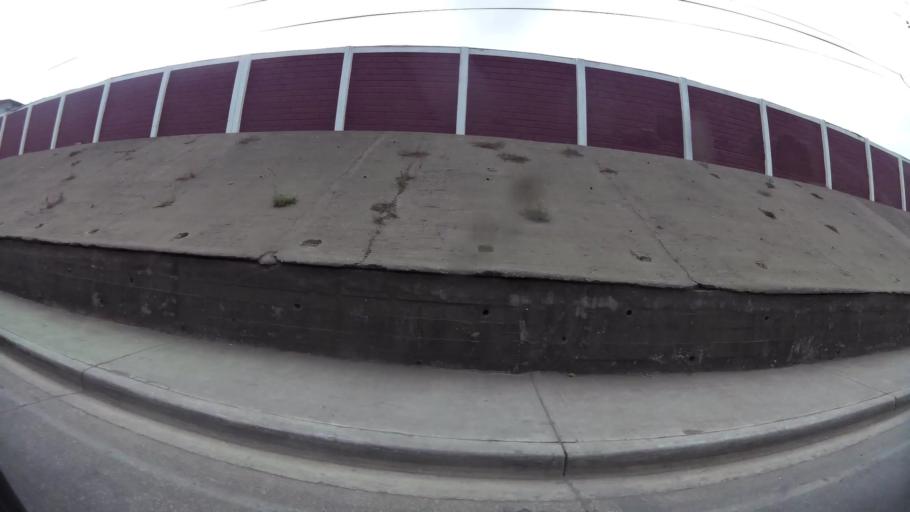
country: EC
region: Guayas
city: Santa Lucia
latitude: -2.1187
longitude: -79.9658
